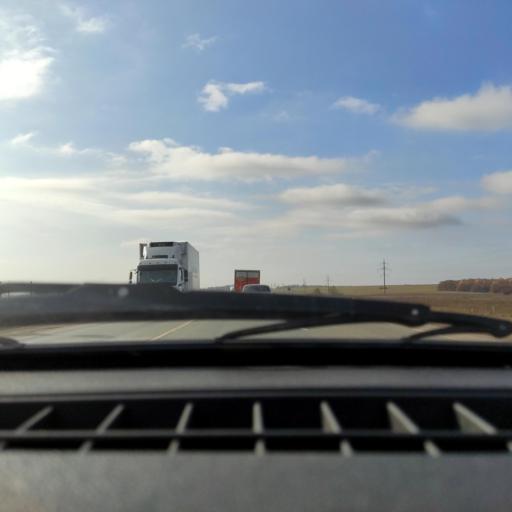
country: RU
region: Bashkortostan
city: Kabakovo
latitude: 54.6983
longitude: 56.2121
